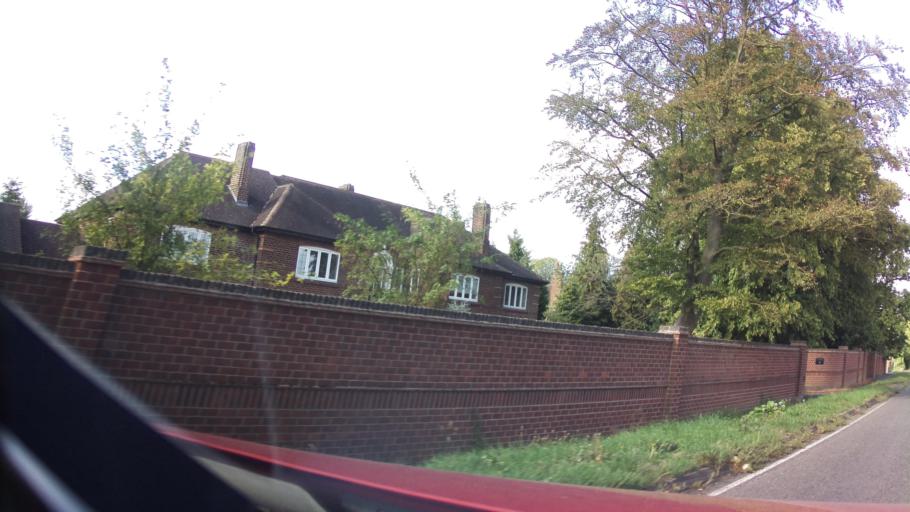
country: GB
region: England
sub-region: Leicestershire
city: Ashby de la Zouch
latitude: 52.7345
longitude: -1.4838
